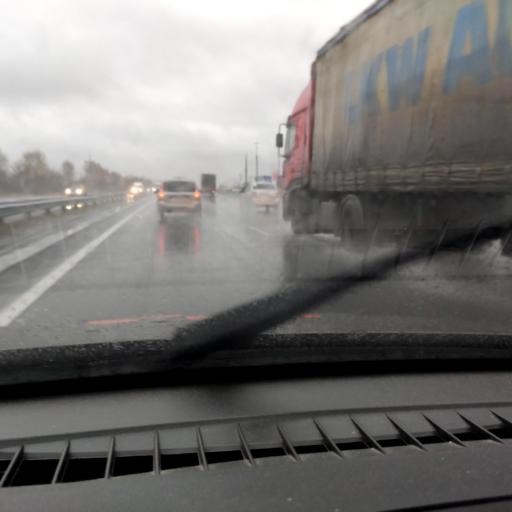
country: RU
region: Samara
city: Tol'yatti
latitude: 53.5788
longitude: 49.4108
